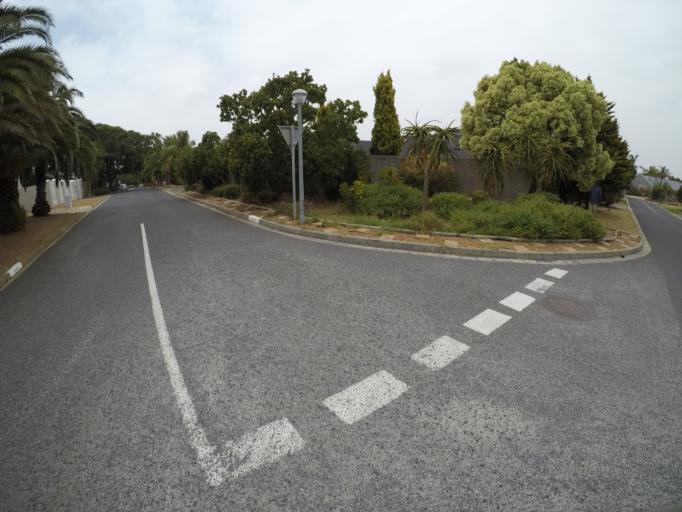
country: ZA
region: Western Cape
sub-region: City of Cape Town
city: Kraaifontein
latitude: -33.8701
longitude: 18.6453
